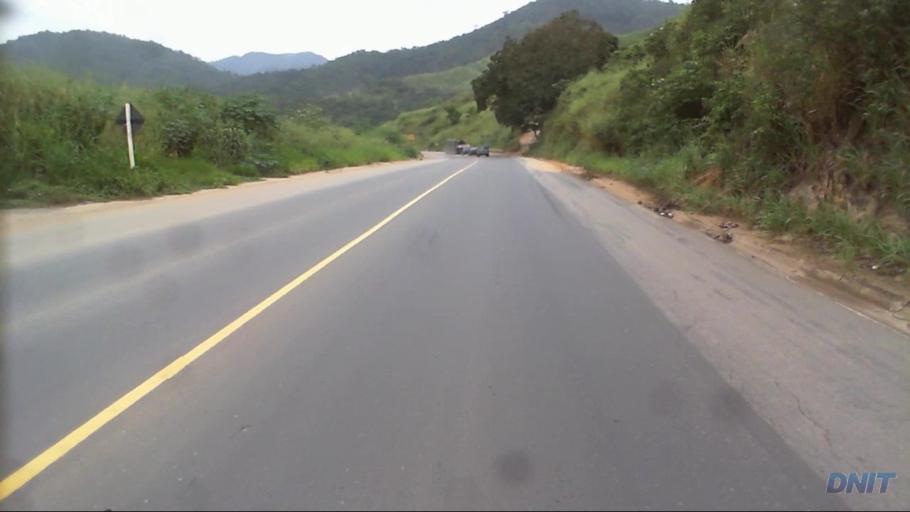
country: BR
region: Minas Gerais
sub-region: Timoteo
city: Timoteo
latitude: -19.5390
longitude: -42.6803
